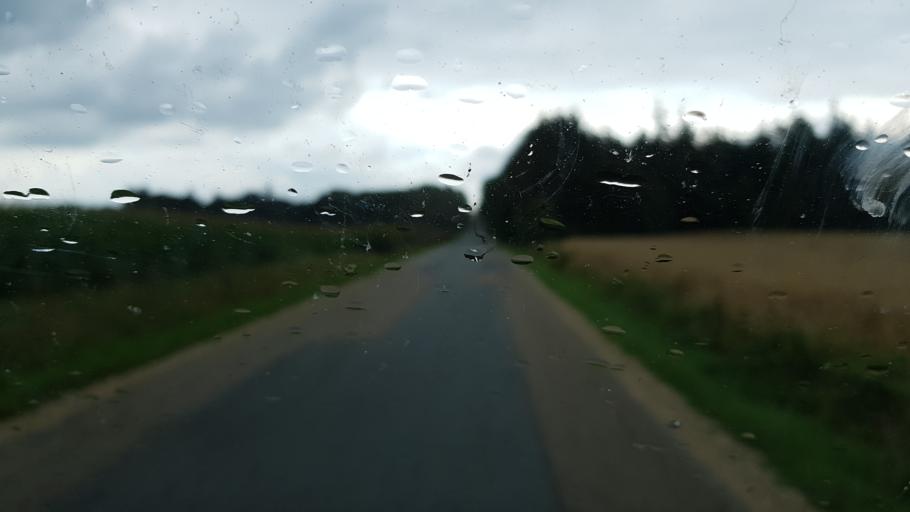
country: DK
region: South Denmark
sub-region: Billund Kommune
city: Grindsted
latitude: 55.6416
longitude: 8.8245
